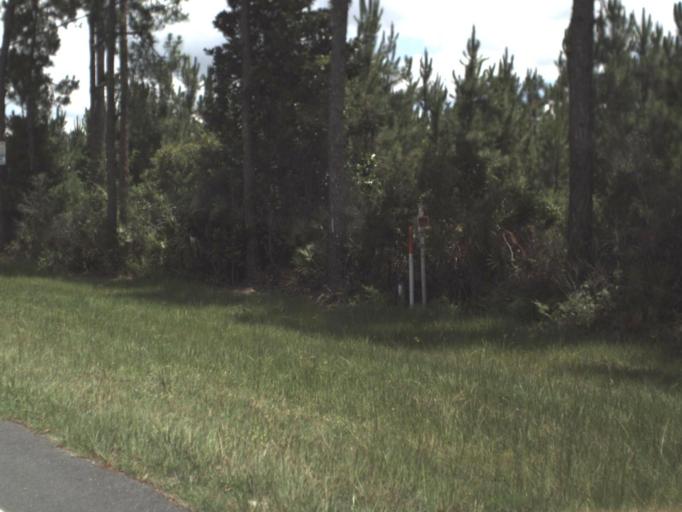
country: US
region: Florida
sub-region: Clay County
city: Keystone Heights
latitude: 29.7137
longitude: -82.0445
